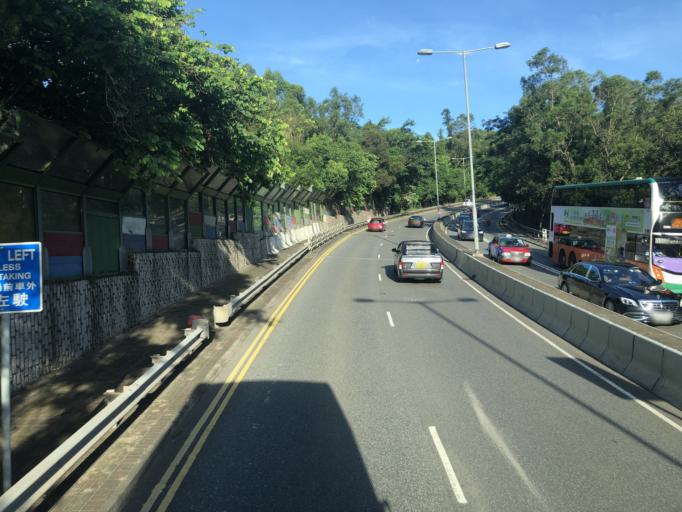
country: HK
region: Sai Kung
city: Sai Kung
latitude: 22.3516
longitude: 114.2526
